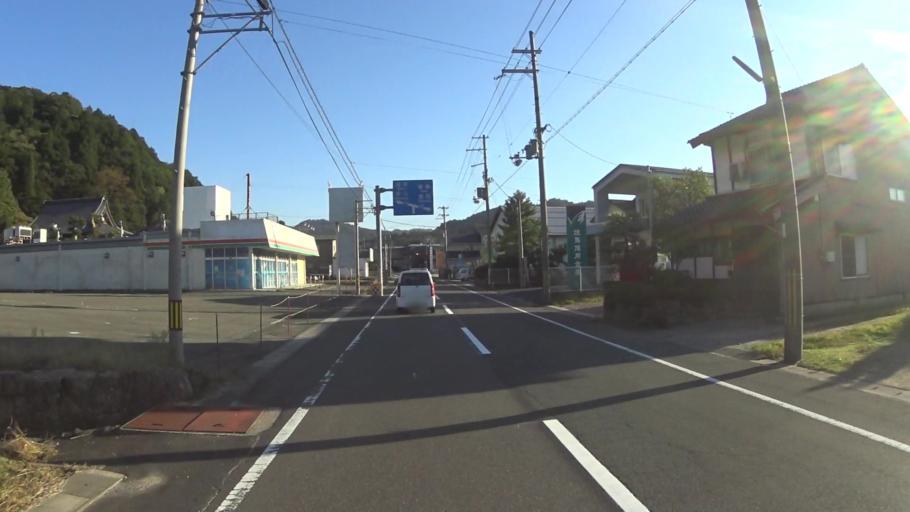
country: JP
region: Hyogo
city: Toyooka
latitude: 35.6037
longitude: 134.9019
